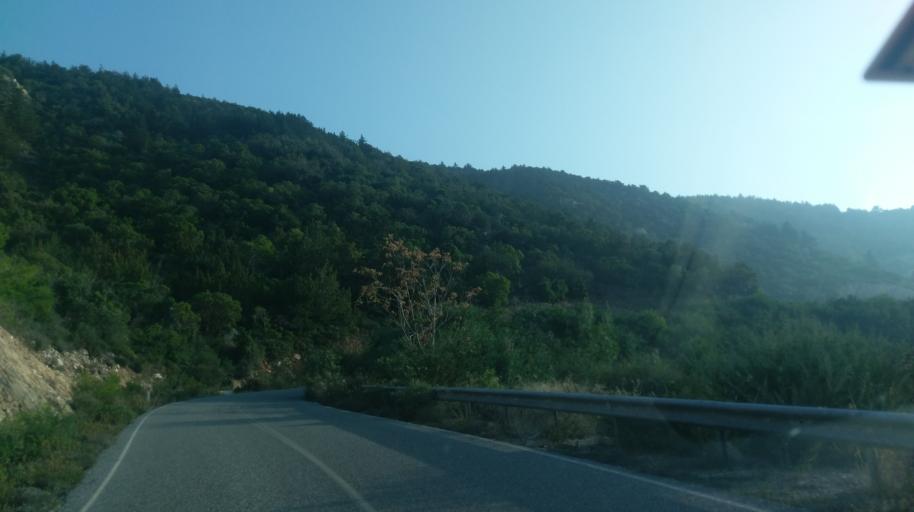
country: CY
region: Ammochostos
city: Trikomo
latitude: 35.4027
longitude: 33.9042
